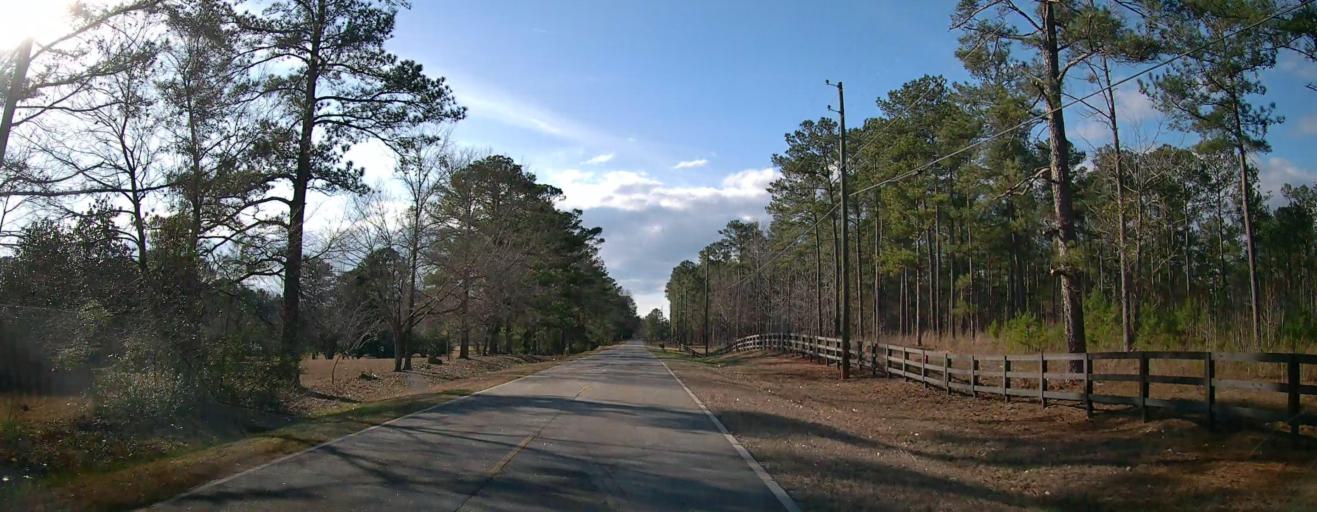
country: US
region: Georgia
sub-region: Harris County
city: Hamilton
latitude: 32.5602
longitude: -84.7861
